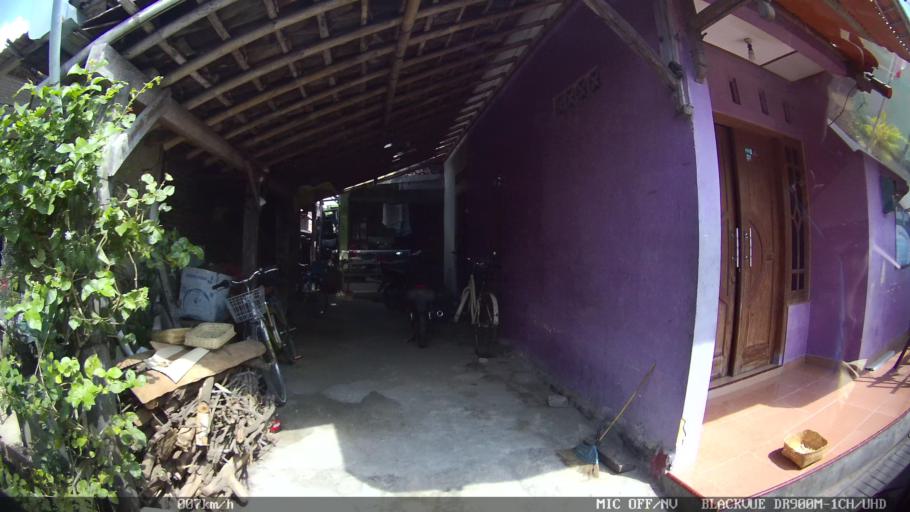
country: ID
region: Daerah Istimewa Yogyakarta
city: Kasihan
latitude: -7.8337
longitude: 110.3723
